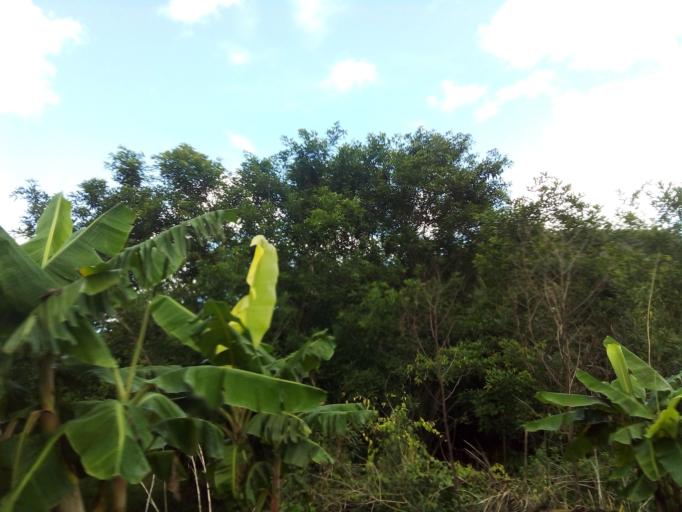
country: BR
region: Espirito Santo
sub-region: Ibiracu
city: Ibiracu
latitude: -19.8656
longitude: -40.3615
